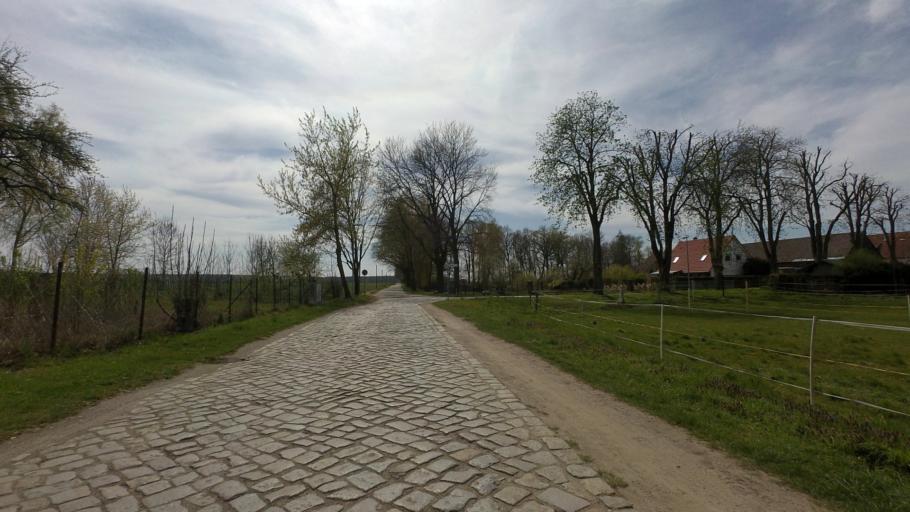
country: DE
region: Brandenburg
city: Schulzendorf
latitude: 52.3363
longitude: 13.5432
